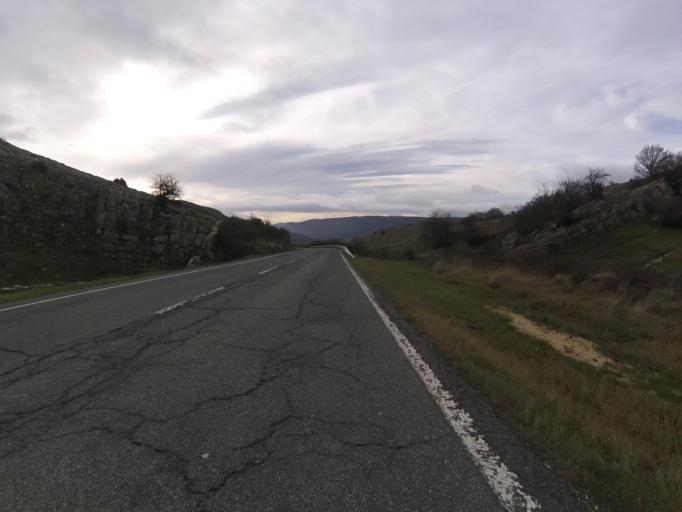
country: ES
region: Navarre
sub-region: Provincia de Navarra
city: Arbizu
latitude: 42.8581
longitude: -2.0125
